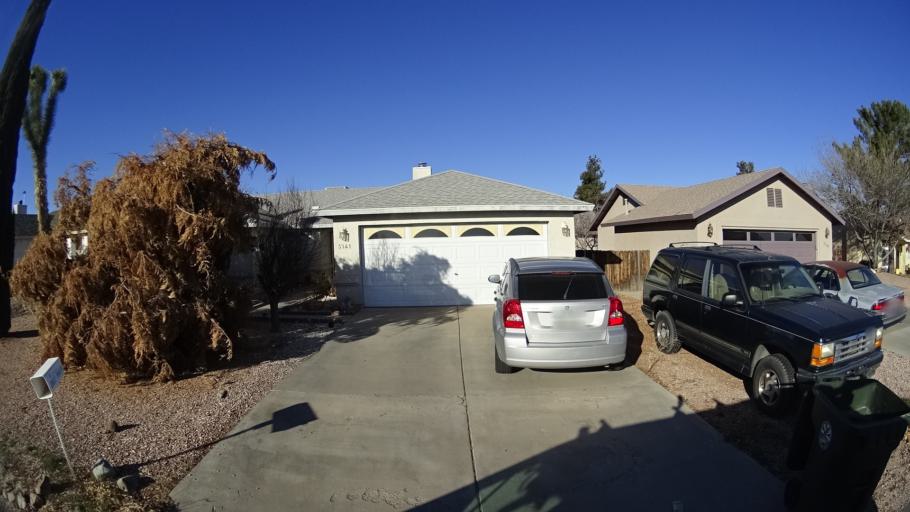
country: US
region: Arizona
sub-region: Mohave County
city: Kingman
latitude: 35.2145
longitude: -114.0085
